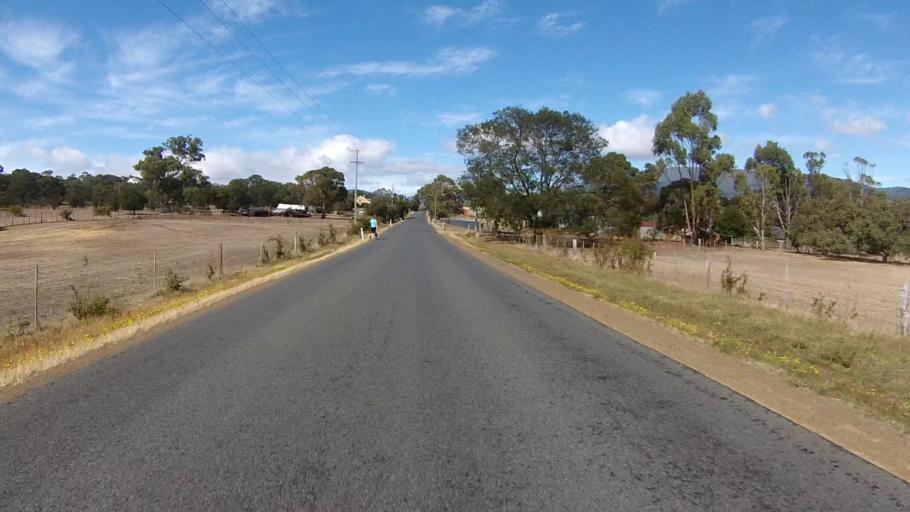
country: AU
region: Tasmania
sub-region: Brighton
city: Old Beach
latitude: -42.7657
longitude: 147.2758
